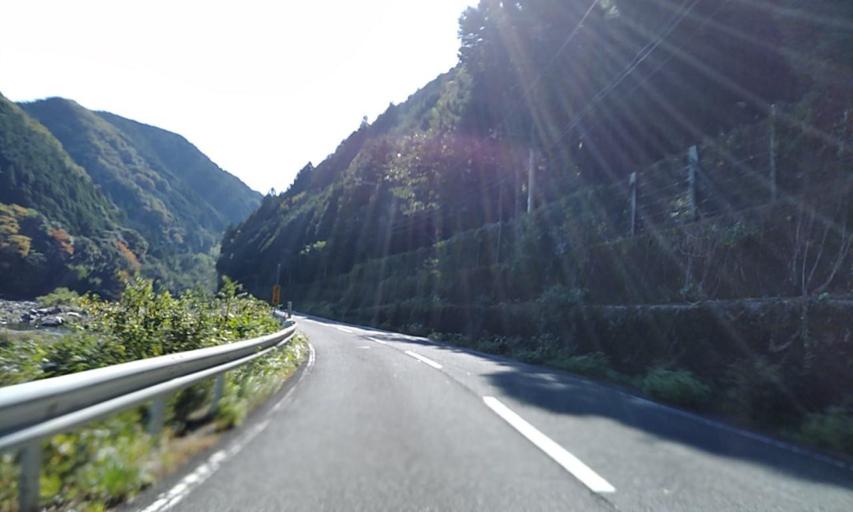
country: JP
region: Wakayama
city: Kainan
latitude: 34.0598
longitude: 135.3507
